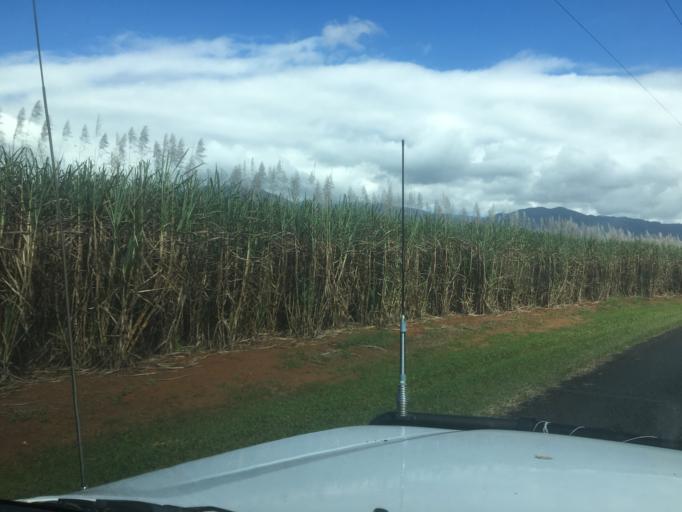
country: AU
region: Queensland
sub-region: Cassowary Coast
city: Innisfail
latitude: -17.3504
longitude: 145.8946
